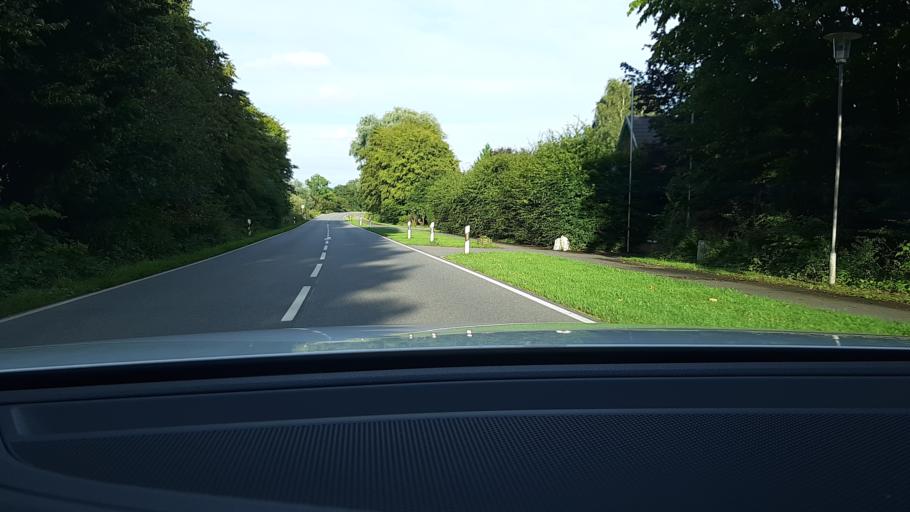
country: DE
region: Schleswig-Holstein
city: Monkhagen
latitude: 53.9116
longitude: 10.5286
